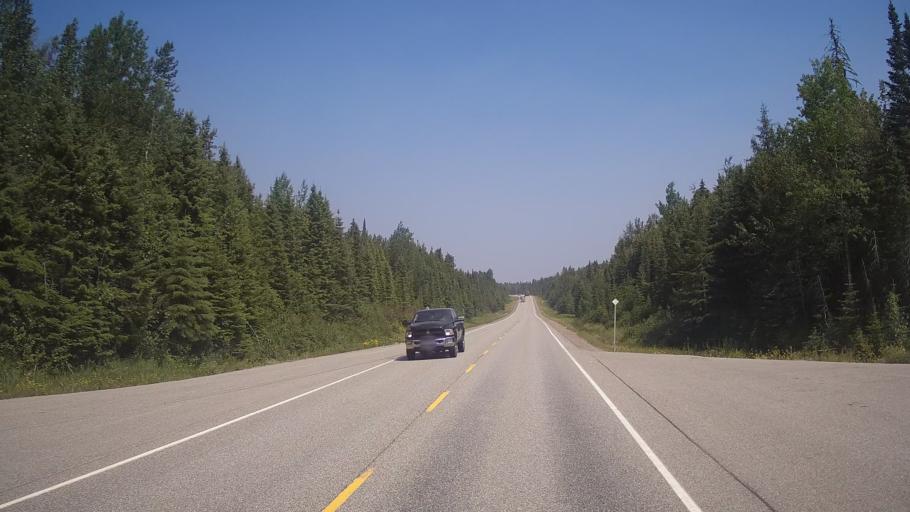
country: CA
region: Ontario
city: Timmins
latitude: 48.0934
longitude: -81.5933
